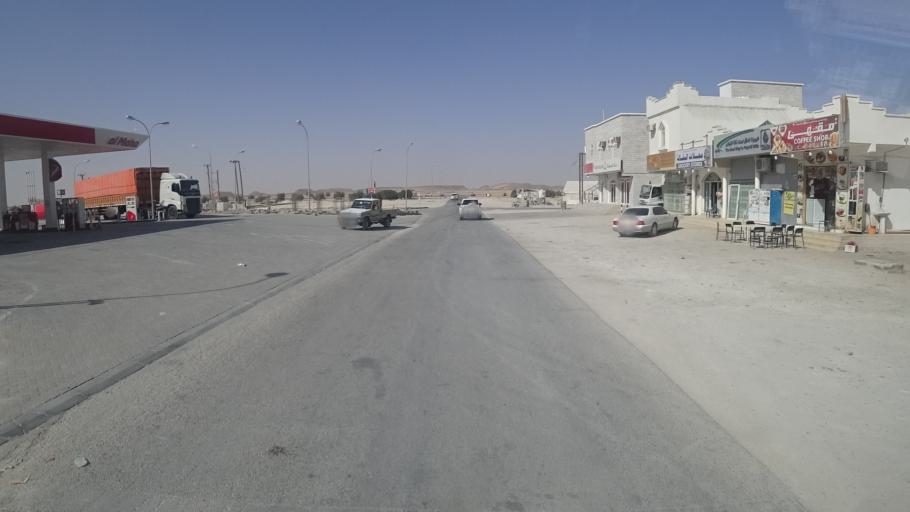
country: YE
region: Al Mahrah
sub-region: Shahan
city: Shihan as Sufla
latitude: 17.8434
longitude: 52.6640
